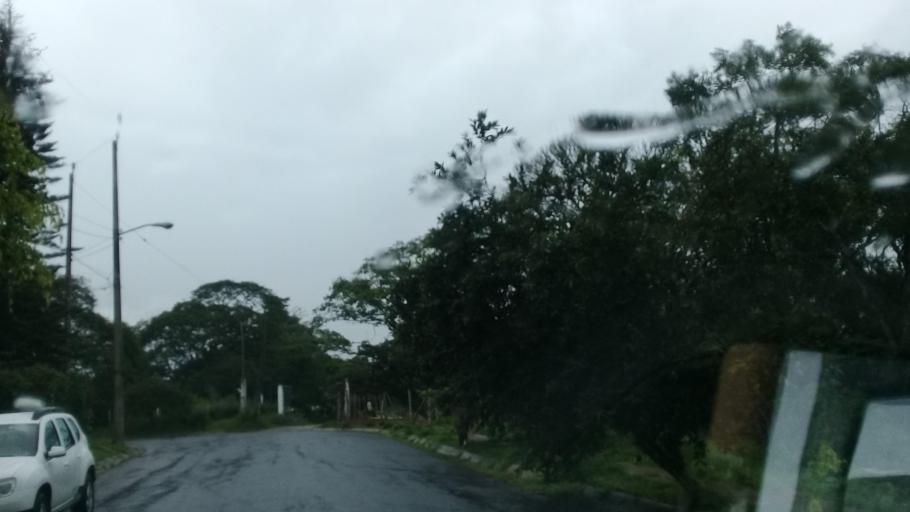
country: MX
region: Veracruz
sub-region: Xalapa
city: Lomas Verdes
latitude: 19.5152
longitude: -96.8998
